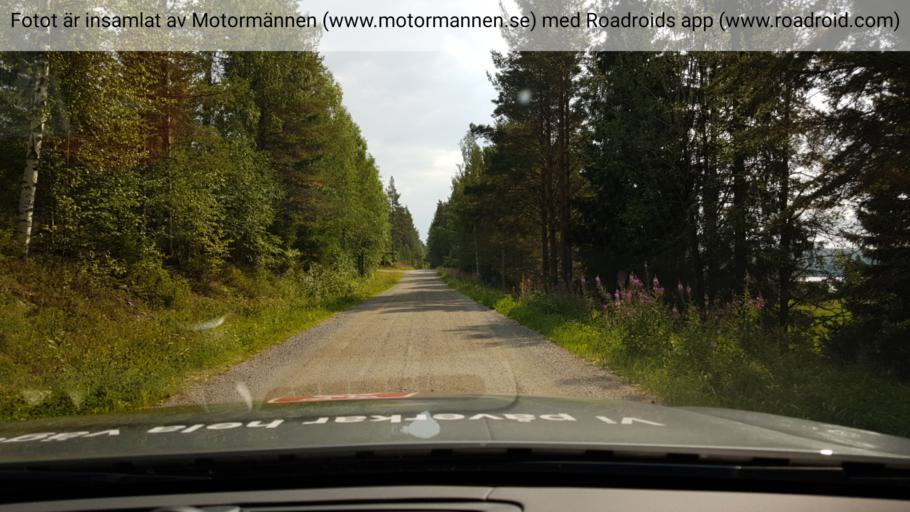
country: SE
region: Jaemtland
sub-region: OEstersunds Kommun
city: Brunflo
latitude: 63.0147
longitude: 15.0978
